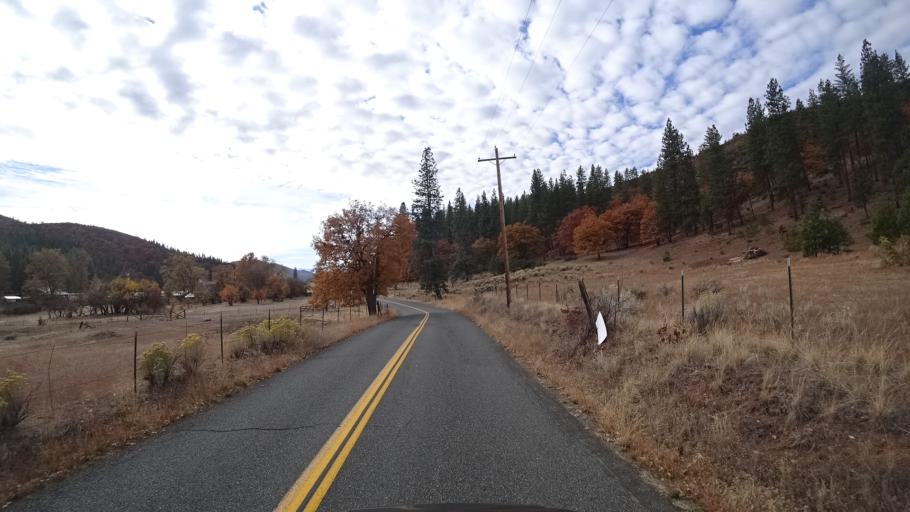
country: US
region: California
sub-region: Siskiyou County
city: Yreka
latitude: 41.6691
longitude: -122.8332
